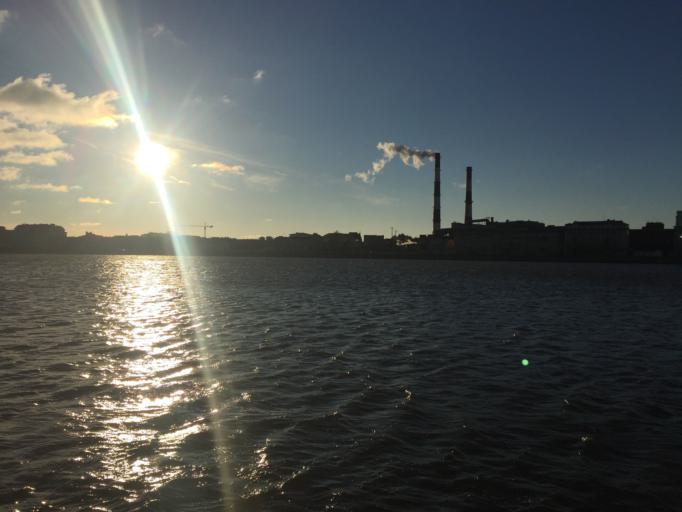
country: RU
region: St.-Petersburg
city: Centralniy
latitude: 59.9341
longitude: 30.4006
